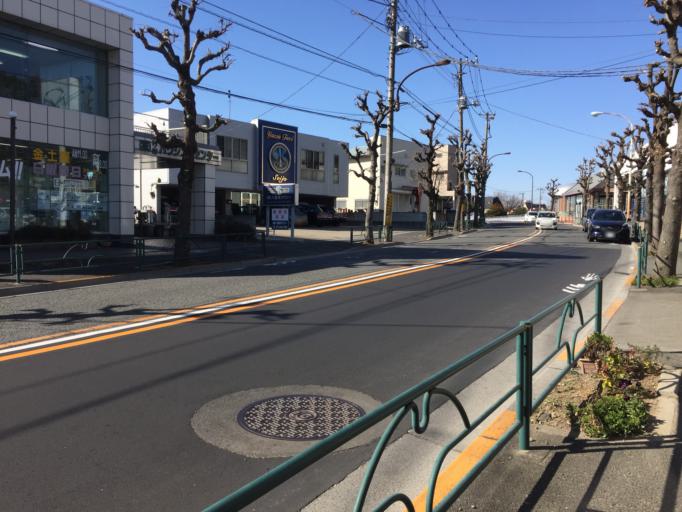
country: JP
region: Tokyo
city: Chofugaoka
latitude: 35.6350
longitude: 139.5951
